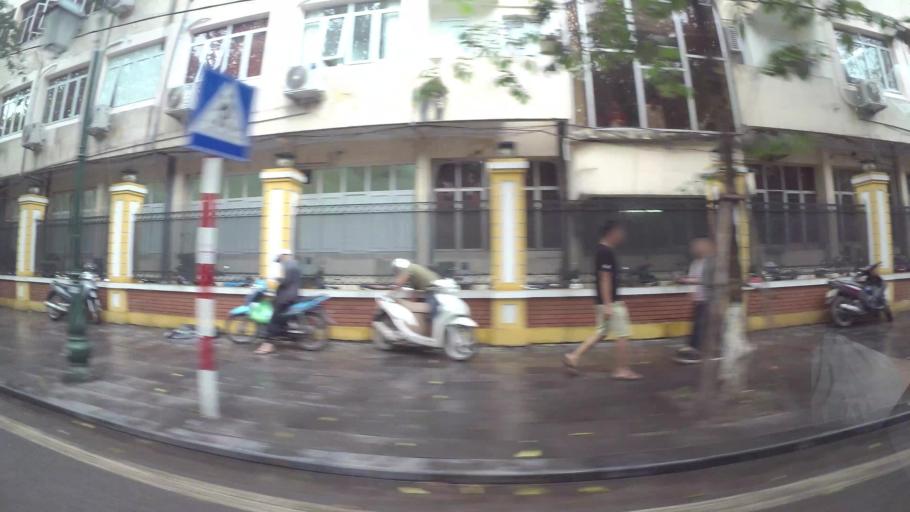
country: VN
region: Ha Noi
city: Hoan Kiem
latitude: 21.0273
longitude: 105.8468
